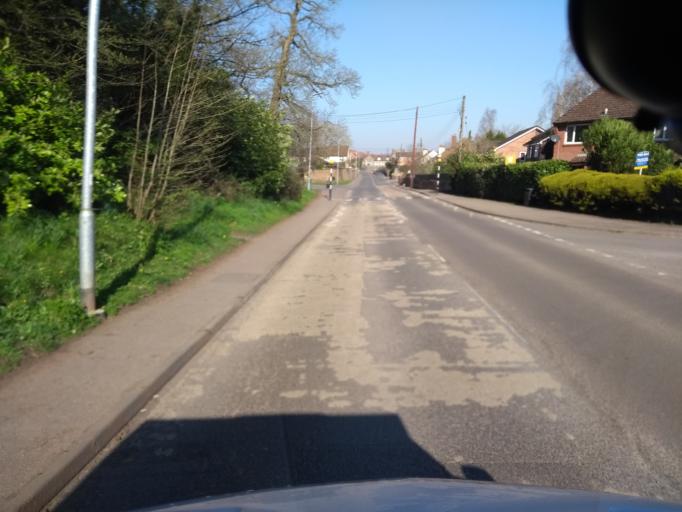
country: GB
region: England
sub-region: Somerset
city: Bishops Lydeard
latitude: 50.9853
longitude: -3.2403
